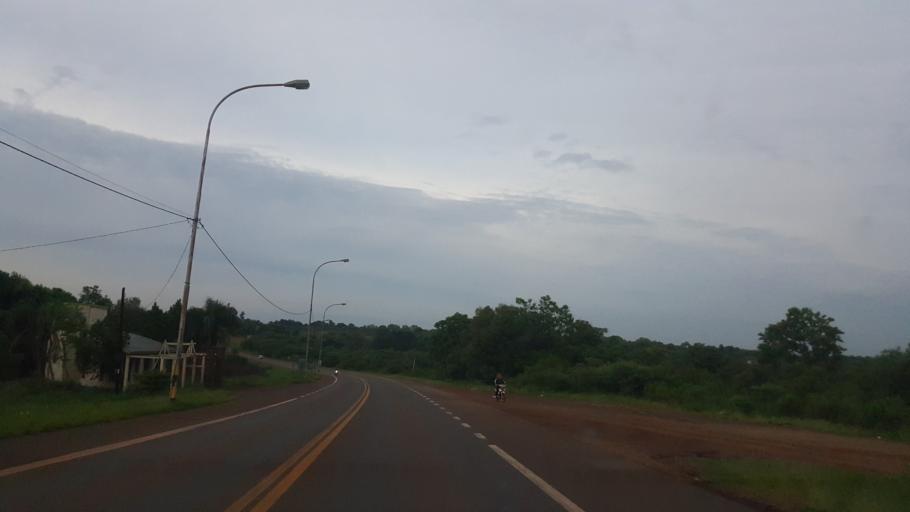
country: AR
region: Misiones
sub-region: Departamento de Apostoles
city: San Jose
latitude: -27.7475
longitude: -55.7829
